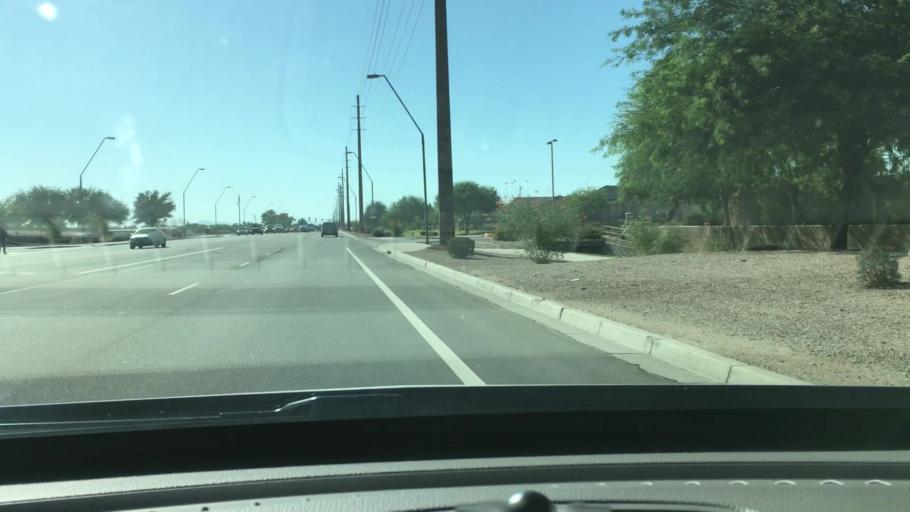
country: US
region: Arizona
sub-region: Maricopa County
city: Queen Creek
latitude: 33.2487
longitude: -111.6122
